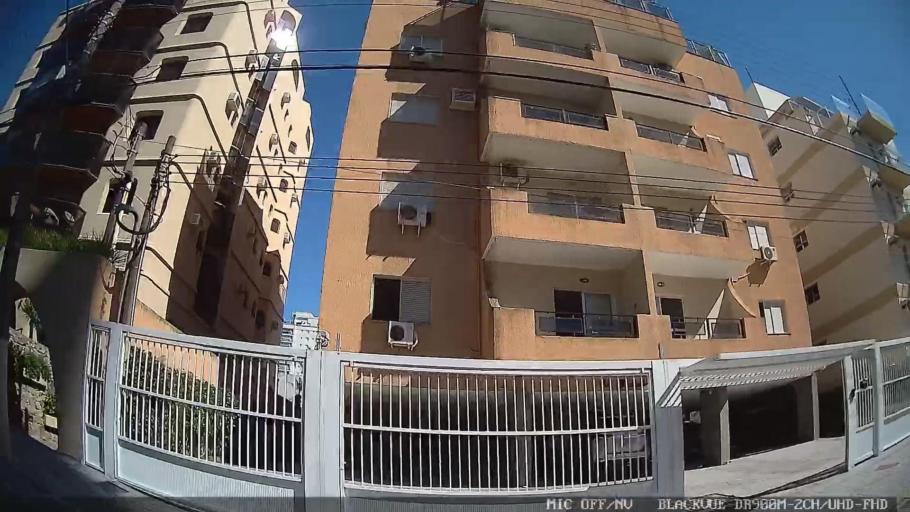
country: BR
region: Sao Paulo
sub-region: Guaruja
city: Guaruja
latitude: -23.9843
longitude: -46.2315
